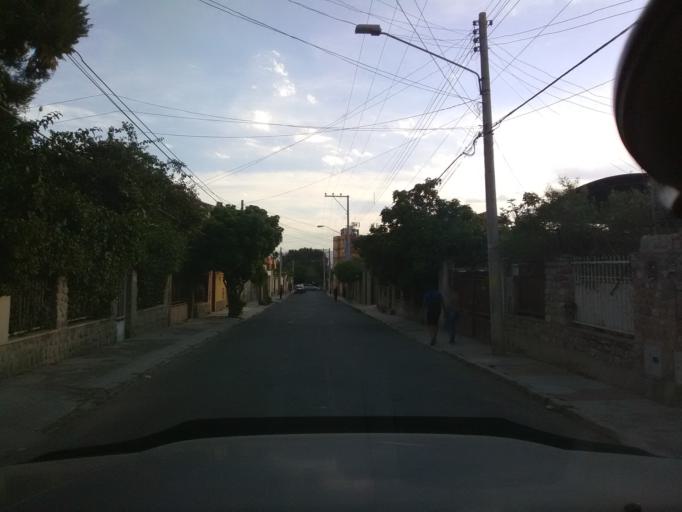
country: BO
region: Cochabamba
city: Cochabamba
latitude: -17.3699
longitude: -66.1842
